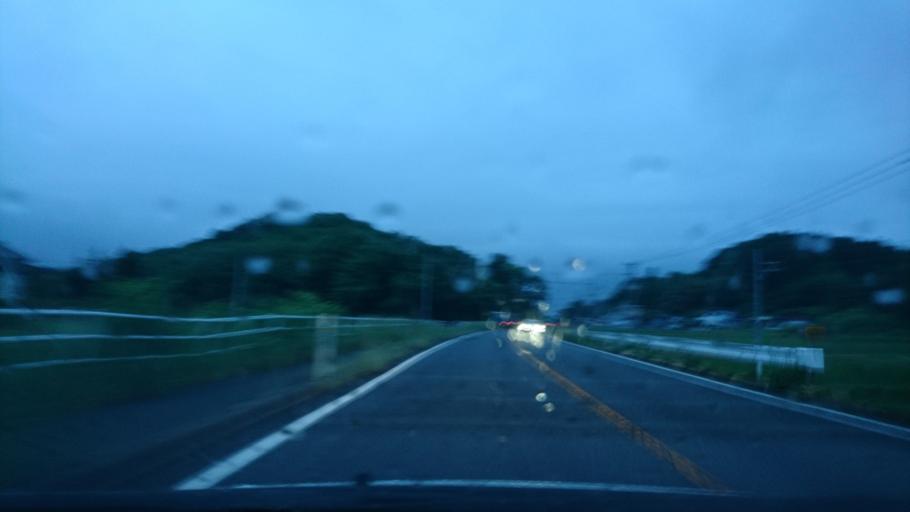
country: JP
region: Iwate
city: Ichinoseki
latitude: 38.7860
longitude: 141.0499
